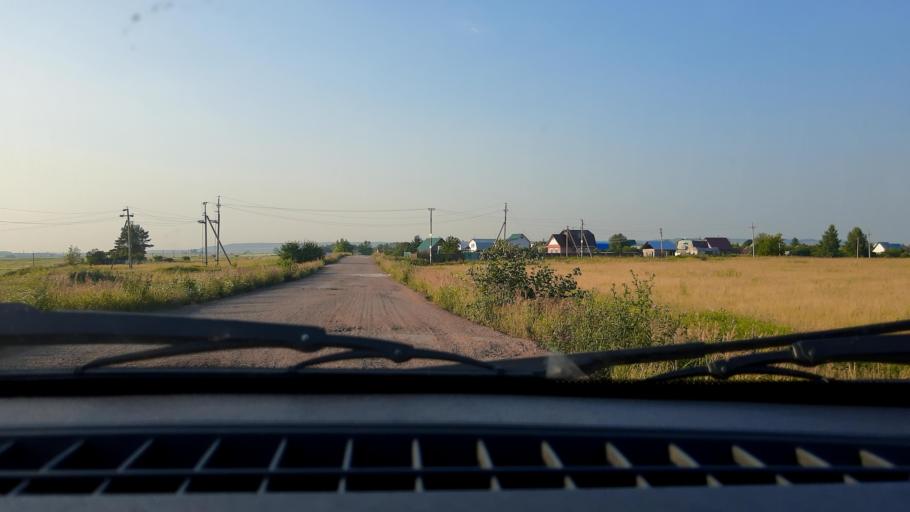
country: RU
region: Bashkortostan
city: Asanovo
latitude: 54.9125
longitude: 55.6270
